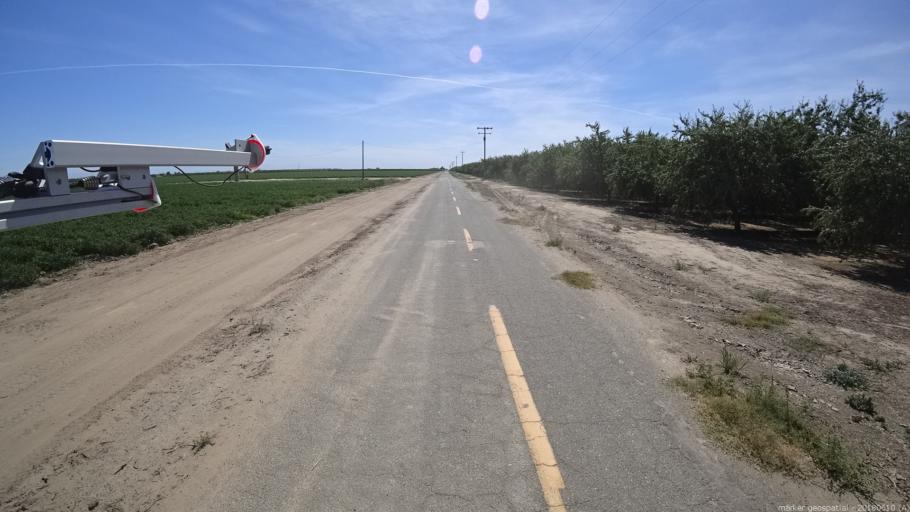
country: US
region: California
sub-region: Madera County
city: Chowchilla
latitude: 37.0253
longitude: -120.3746
